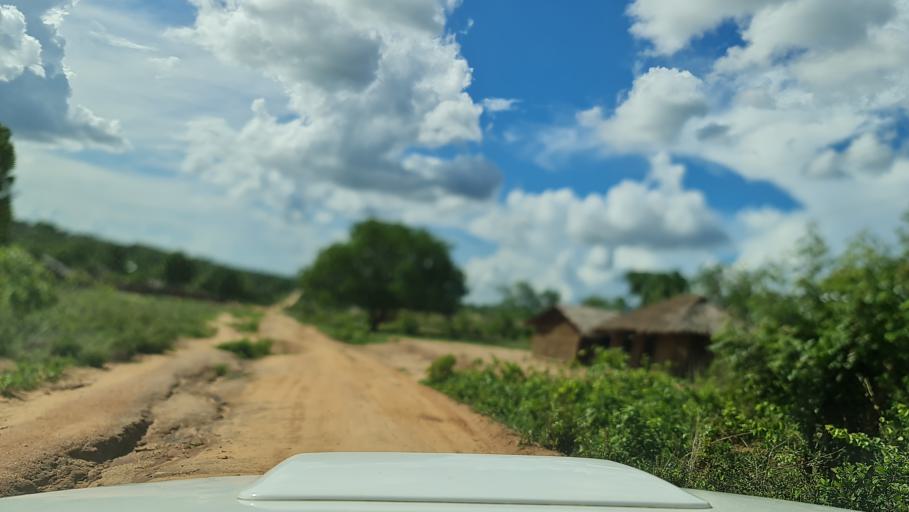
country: MZ
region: Nampula
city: Ilha de Mocambique
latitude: -15.4095
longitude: 40.2466
